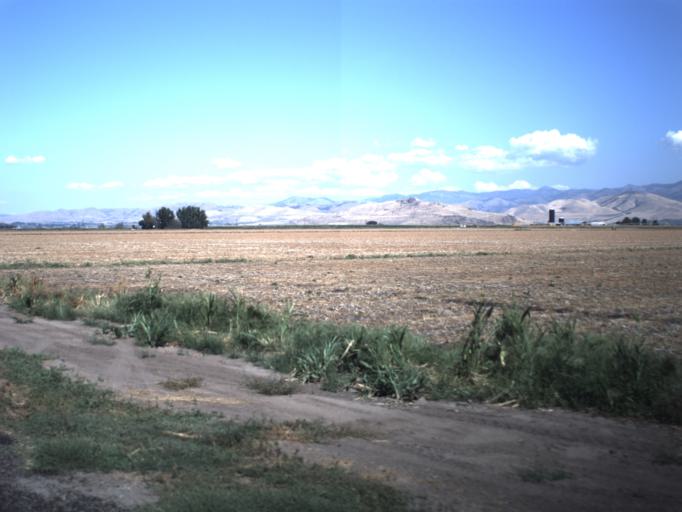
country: US
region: Utah
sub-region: Cache County
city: Lewiston
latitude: 41.9831
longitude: -111.8763
